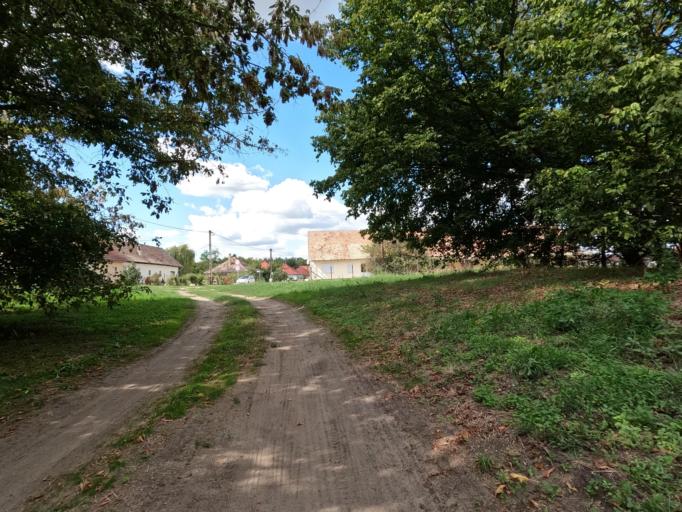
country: HU
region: Tolna
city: Paks
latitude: 46.5906
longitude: 18.8123
